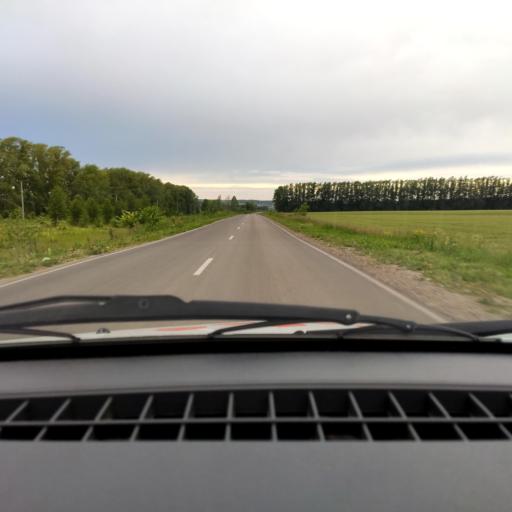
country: RU
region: Bashkortostan
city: Avdon
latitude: 54.5295
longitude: 55.7667
